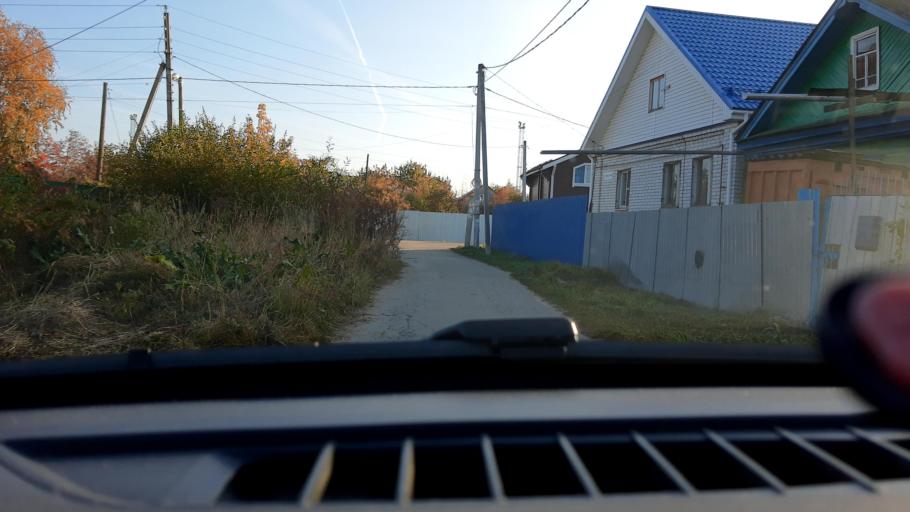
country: RU
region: Nizjnij Novgorod
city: Gorbatovka
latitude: 56.2936
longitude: 43.8575
